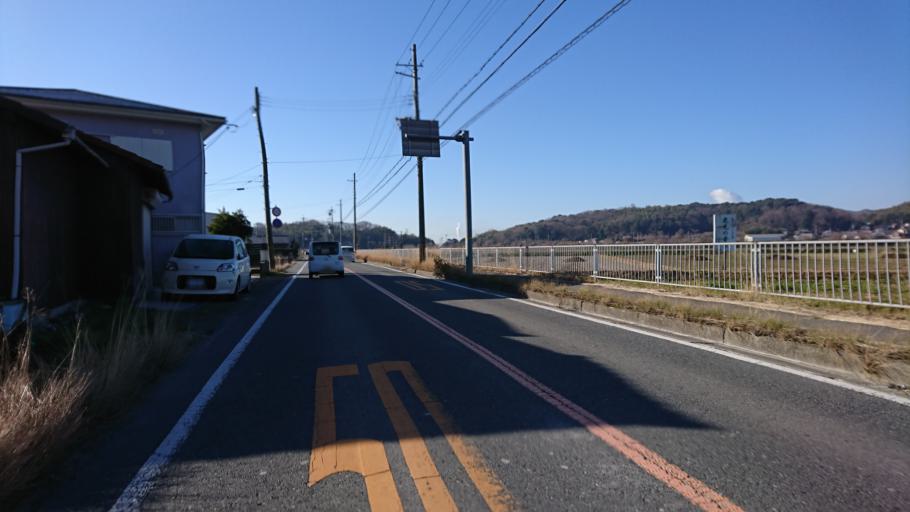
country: JP
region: Hyogo
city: Kakogawacho-honmachi
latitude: 34.8279
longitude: 134.8369
